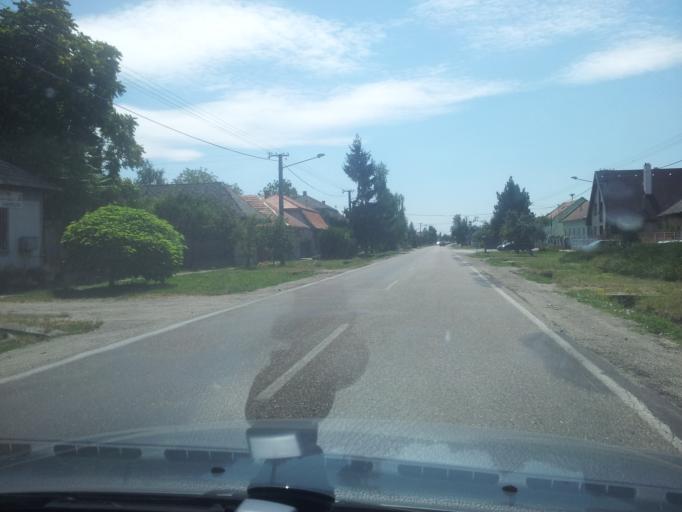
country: SK
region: Nitriansky
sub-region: Okres Nove Zamky
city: Sturovo
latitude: 47.8516
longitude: 18.6557
